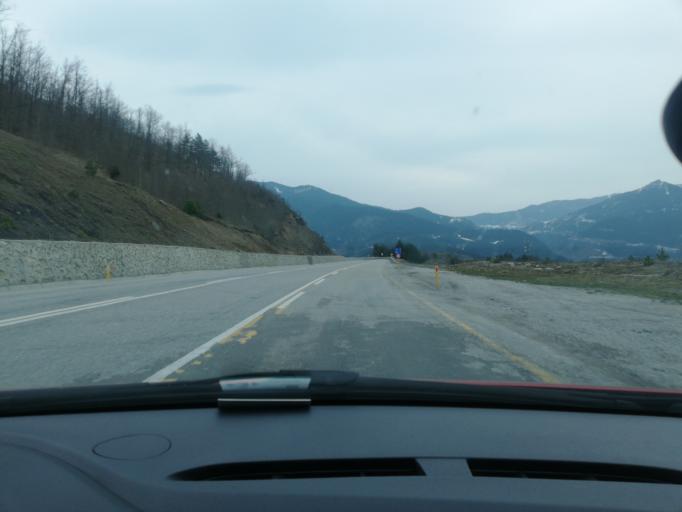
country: TR
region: Kastamonu
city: Kure
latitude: 41.8512
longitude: 33.7134
